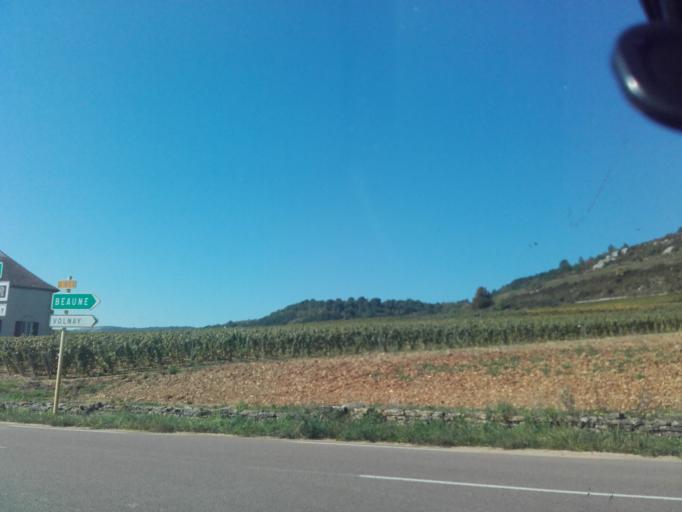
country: FR
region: Bourgogne
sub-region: Departement de la Cote-d'Or
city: Meursault
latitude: 46.9874
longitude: 4.7553
